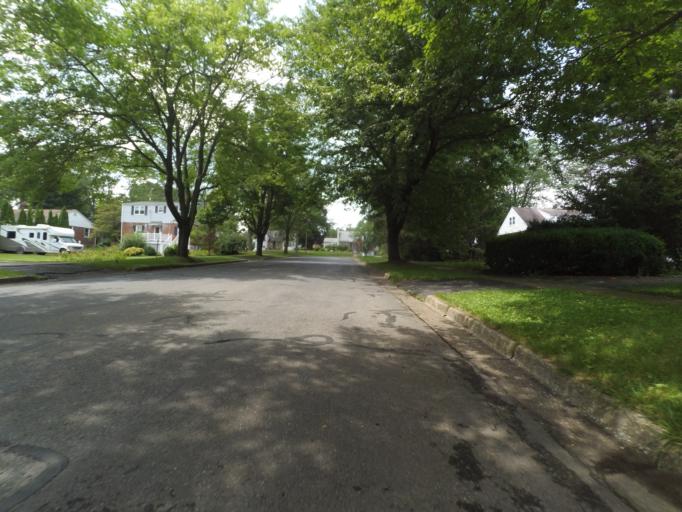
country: US
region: Pennsylvania
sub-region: Centre County
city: State College
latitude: 40.7862
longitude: -77.8453
